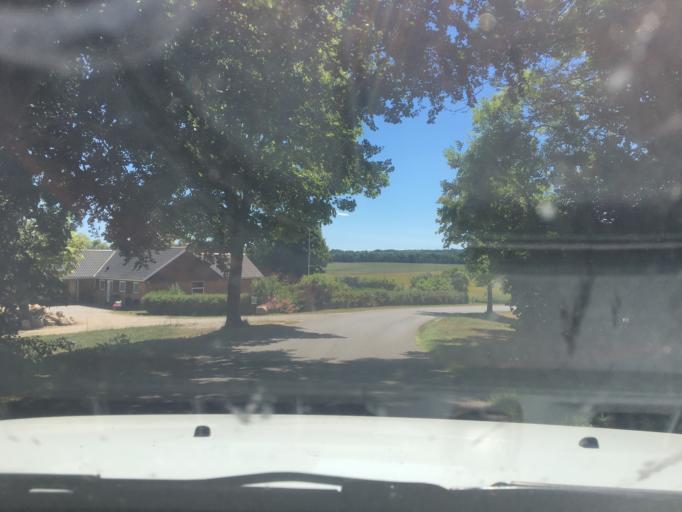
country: DK
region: Central Jutland
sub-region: Syddjurs Kommune
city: Hornslet
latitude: 56.3513
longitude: 10.3889
